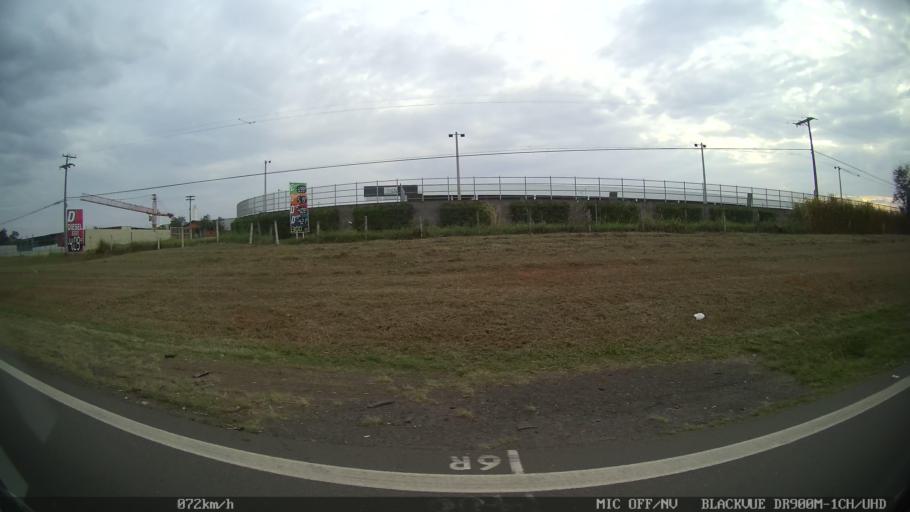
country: BR
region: Sao Paulo
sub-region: Americana
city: Americana
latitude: -22.6430
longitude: -47.3282
